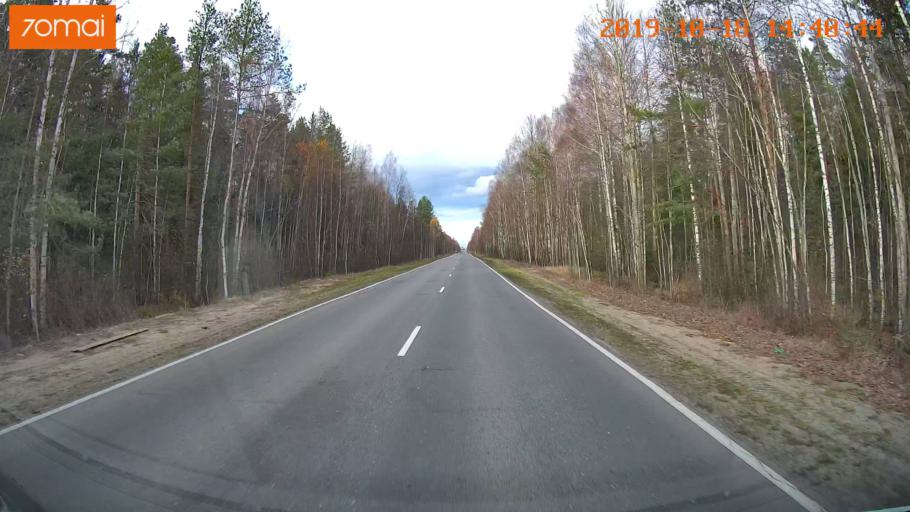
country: RU
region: Vladimir
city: Velikodvorskiy
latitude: 55.2812
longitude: 40.6696
